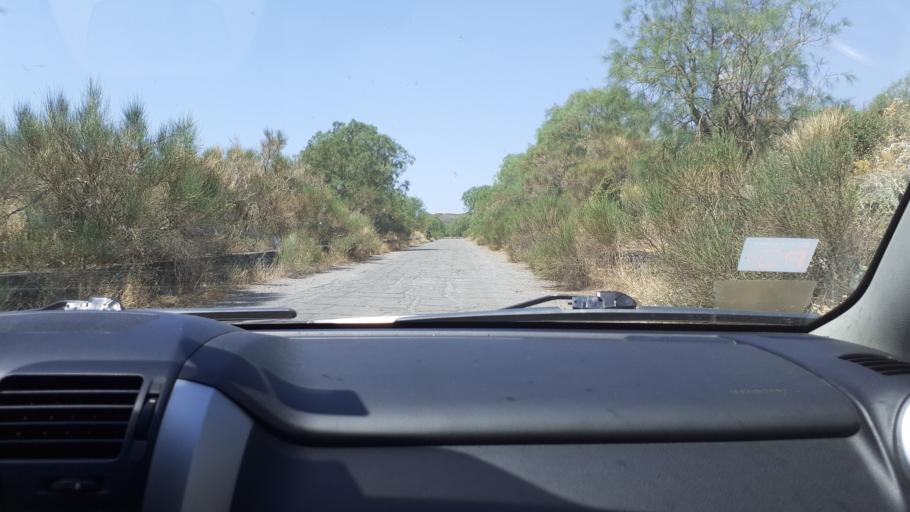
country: IT
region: Sicily
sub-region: Catania
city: Nicolosi
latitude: 37.6462
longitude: 15.0050
